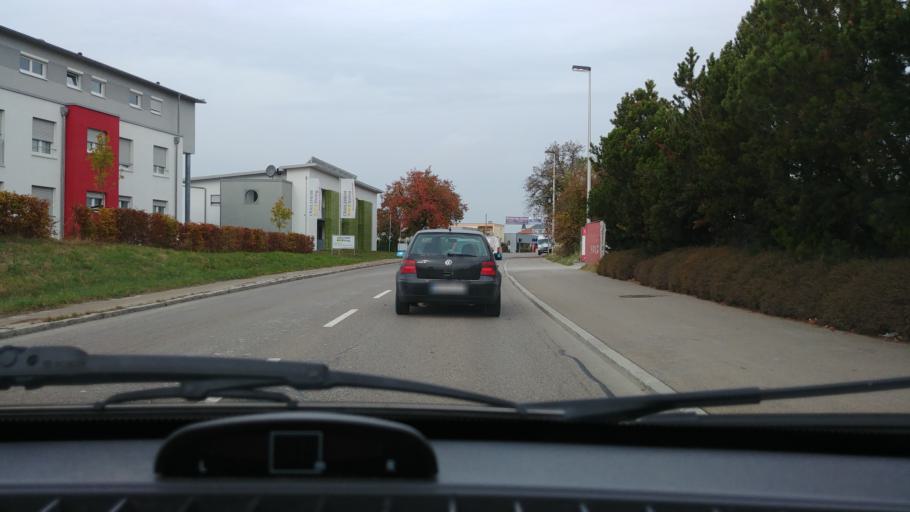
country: DE
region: Baden-Wuerttemberg
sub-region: Regierungsbezirk Stuttgart
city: Crailsheim
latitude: 49.1276
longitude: 10.0798
